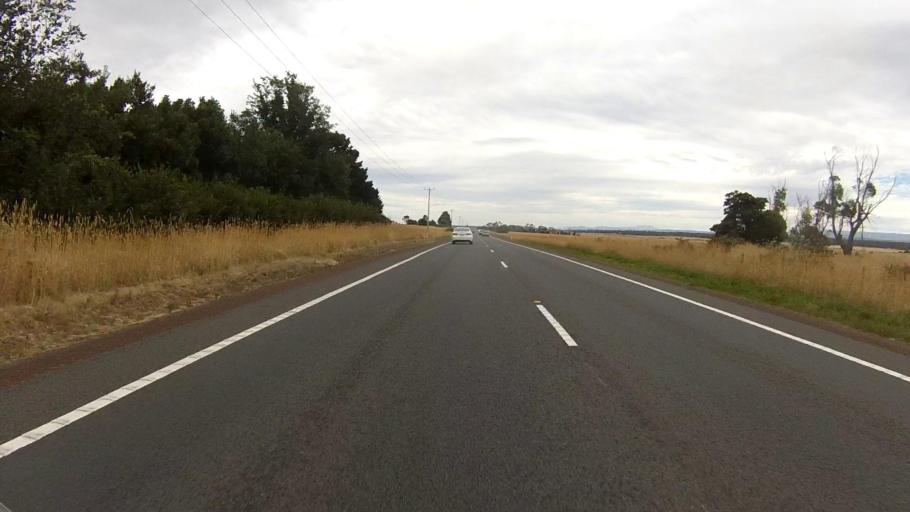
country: AU
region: Tasmania
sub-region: Northern Midlands
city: Evandale
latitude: -41.9014
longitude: 147.4765
